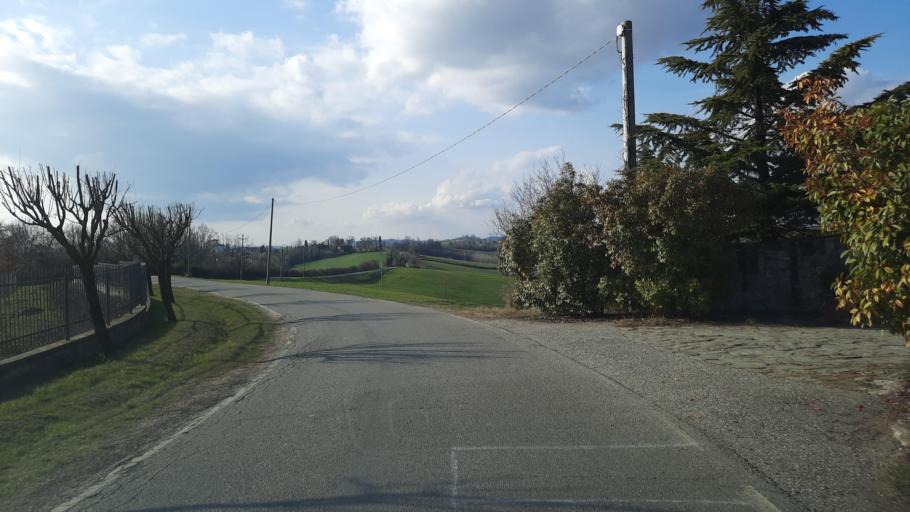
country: IT
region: Piedmont
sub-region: Provincia di Alessandria
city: San Giorgio
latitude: 45.1158
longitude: 8.3964
